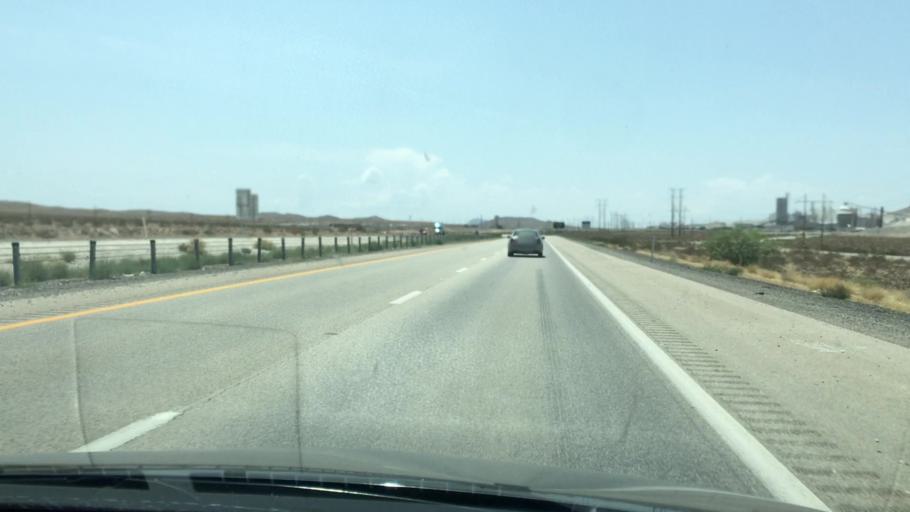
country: US
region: Nevada
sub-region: Clark County
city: Nellis Air Force Base
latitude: 36.3663
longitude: -114.9010
